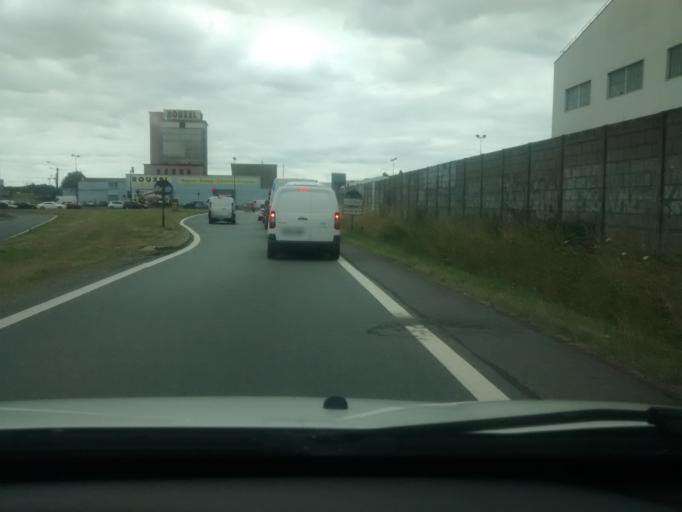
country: FR
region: Brittany
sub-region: Departement d'Ille-et-Vilaine
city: Vezin-le-Coquet
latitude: 48.1084
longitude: -1.7189
